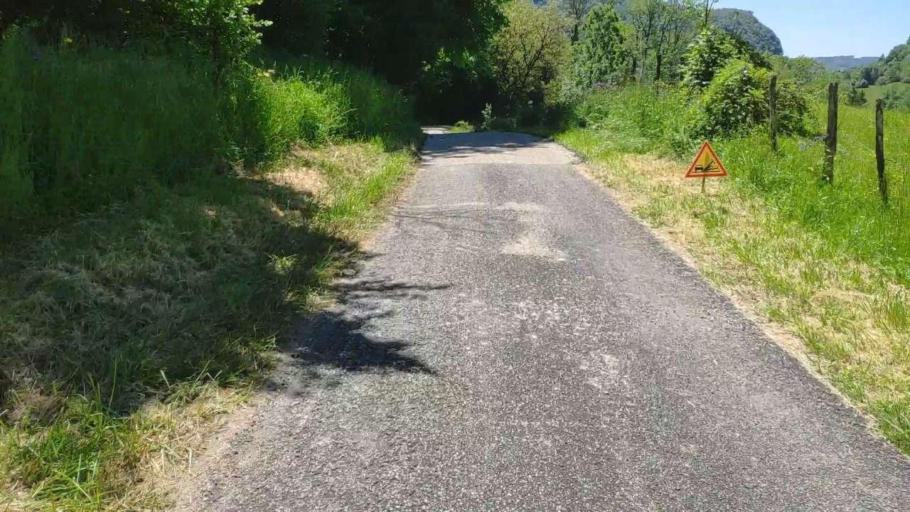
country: FR
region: Franche-Comte
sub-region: Departement du Jura
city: Poligny
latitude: 46.7559
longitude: 5.6760
